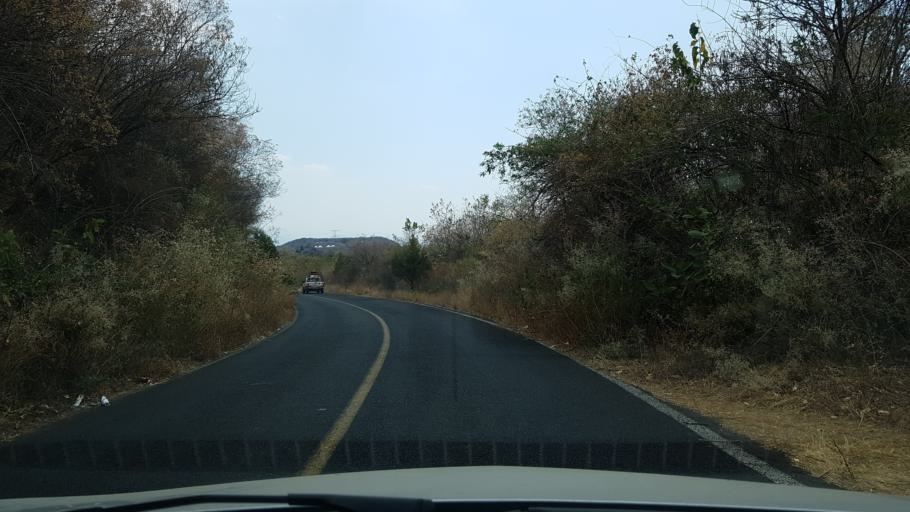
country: MX
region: Morelos
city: Tlacotepec
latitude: 18.8361
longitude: -98.7342
